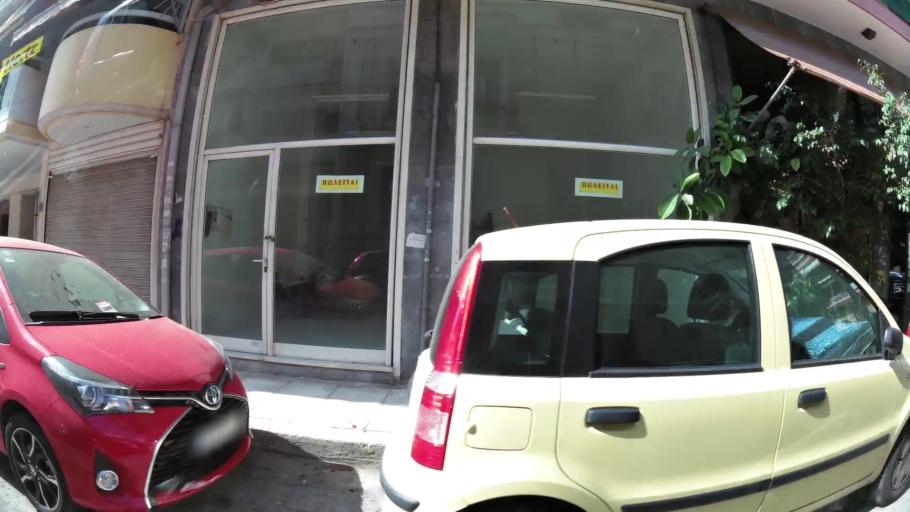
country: GR
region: Attica
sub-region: Nomarchia Athinas
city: Athens
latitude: 37.9909
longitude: 23.7181
